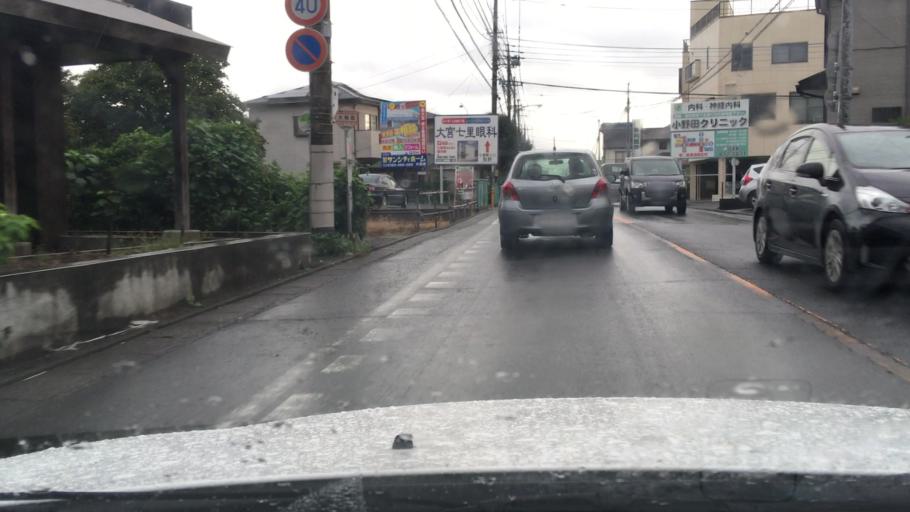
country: JP
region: Saitama
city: Saitama
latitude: 35.9194
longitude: 139.6482
